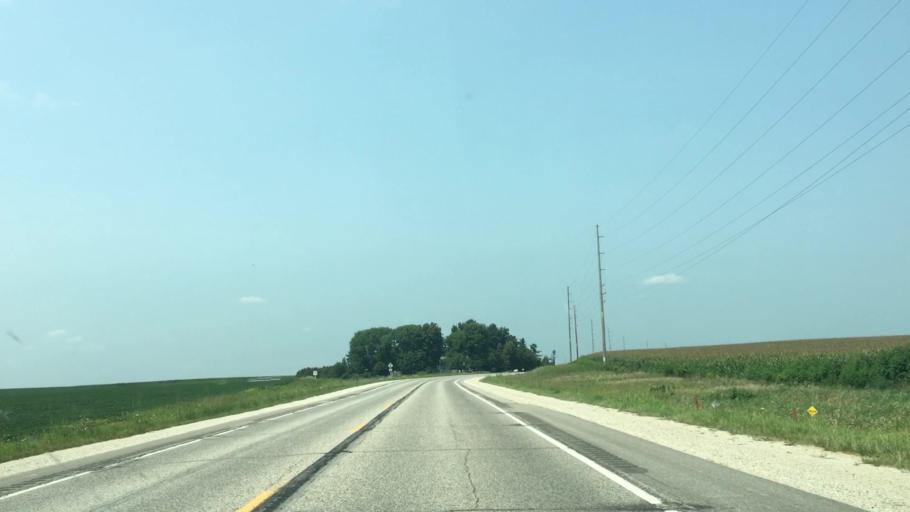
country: US
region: Iowa
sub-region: Fayette County
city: West Union
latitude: 42.9088
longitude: -91.8133
